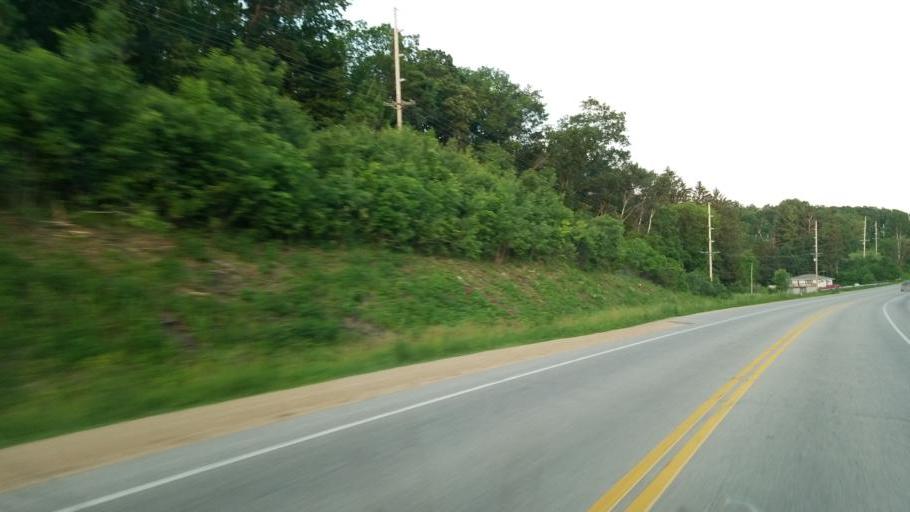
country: US
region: Wisconsin
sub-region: Monroe County
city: Tomah
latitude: 43.8216
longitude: -90.4400
